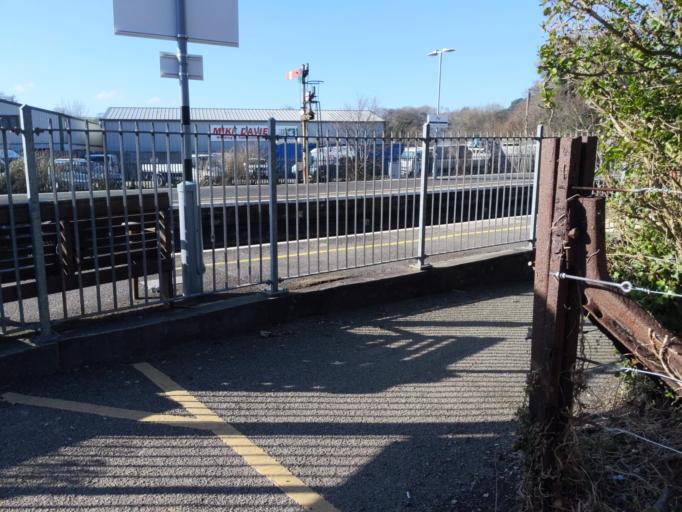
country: GB
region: England
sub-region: Cornwall
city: Par
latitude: 50.3562
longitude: -4.7043
